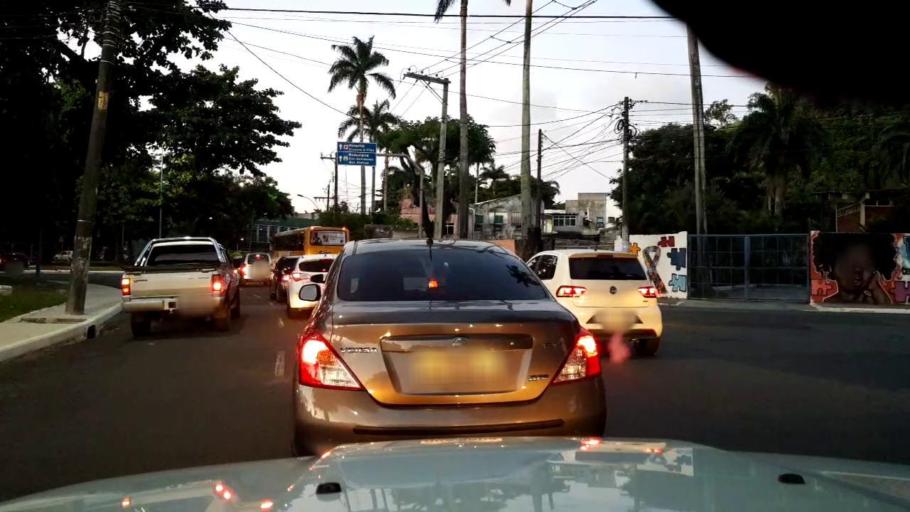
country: BR
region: Bahia
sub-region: Salvador
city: Salvador
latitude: -13.0060
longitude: -38.5091
